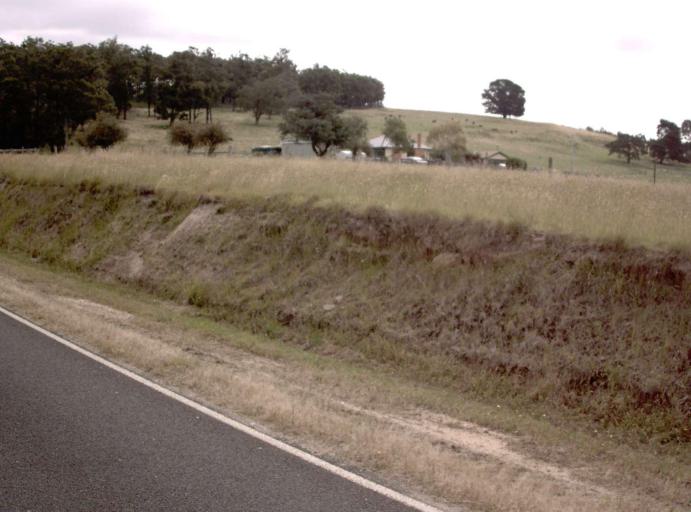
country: AU
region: Victoria
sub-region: Latrobe
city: Traralgon
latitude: -38.4100
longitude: 146.8208
